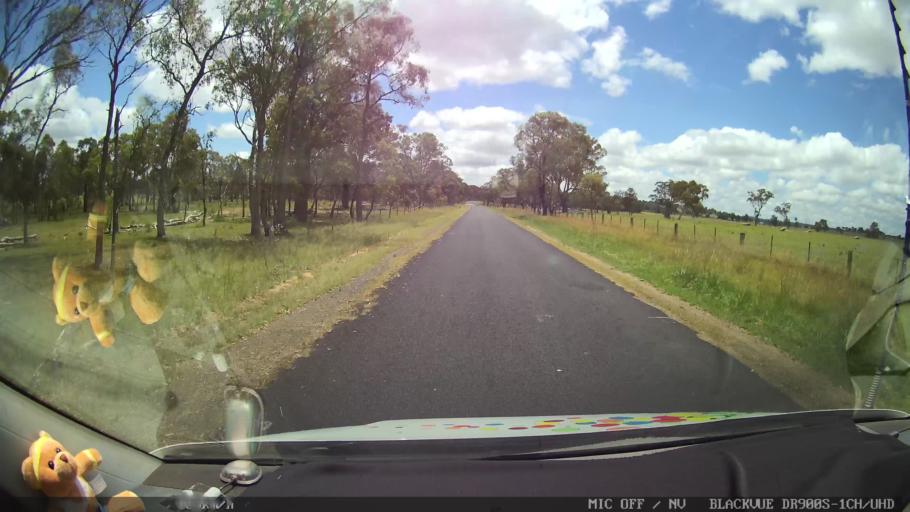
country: AU
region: New South Wales
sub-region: Glen Innes Severn
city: Glen Innes
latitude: -29.4203
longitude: 151.7270
